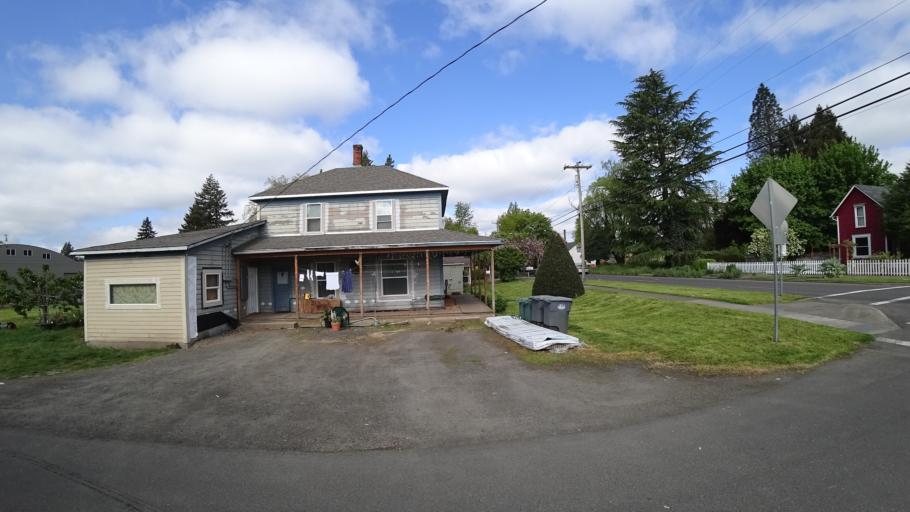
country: US
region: Oregon
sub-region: Washington County
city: Hillsboro
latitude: 45.5174
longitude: -122.9845
